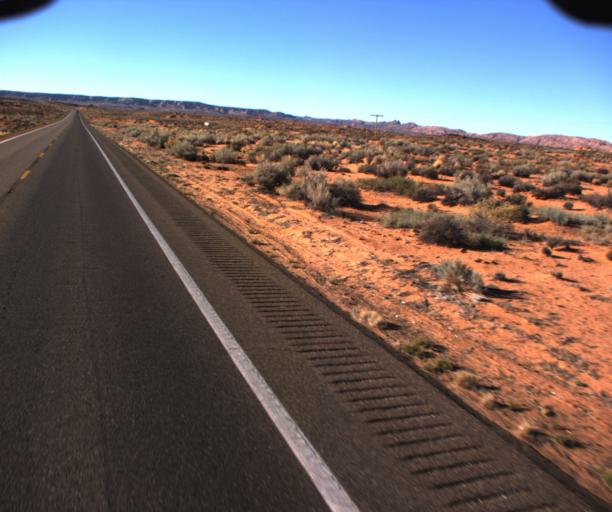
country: US
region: Arizona
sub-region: Coconino County
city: LeChee
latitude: 36.8583
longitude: -111.5059
